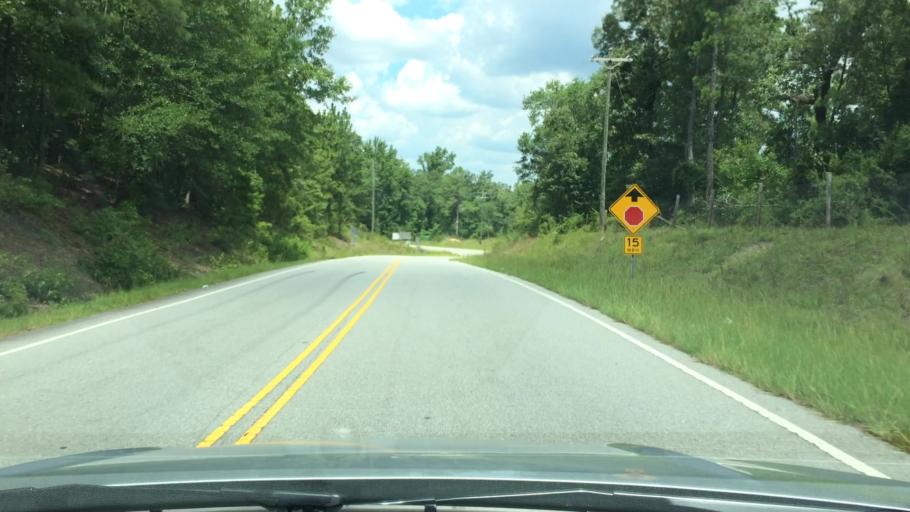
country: US
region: South Carolina
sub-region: Calhoun County
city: Oak Grove
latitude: 33.8102
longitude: -81.0094
